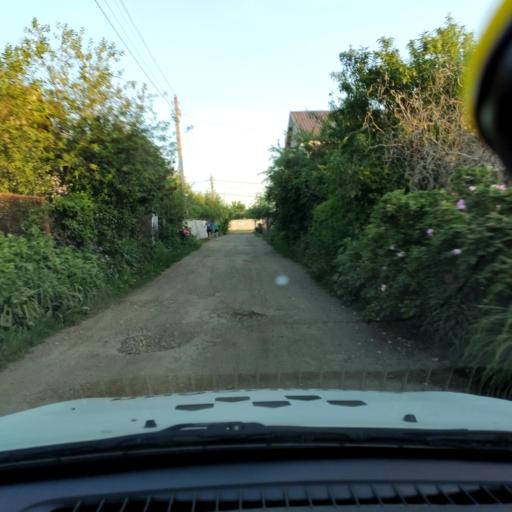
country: RU
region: Samara
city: Podstepki
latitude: 53.5977
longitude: 49.2278
